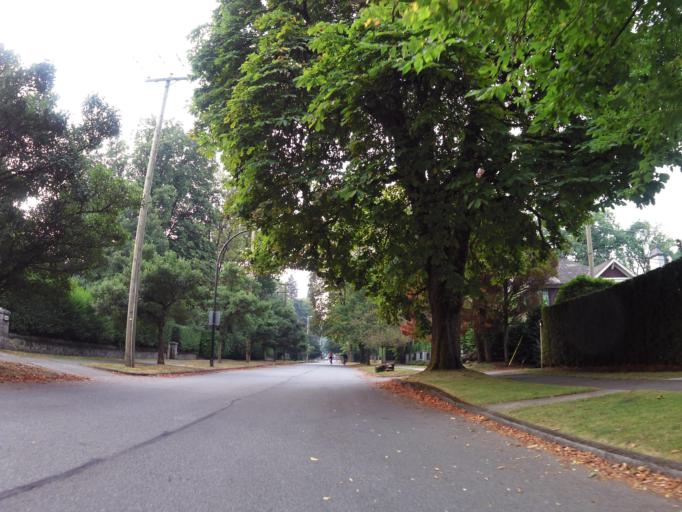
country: CA
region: British Columbia
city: Vancouver
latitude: 49.2561
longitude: -123.1485
